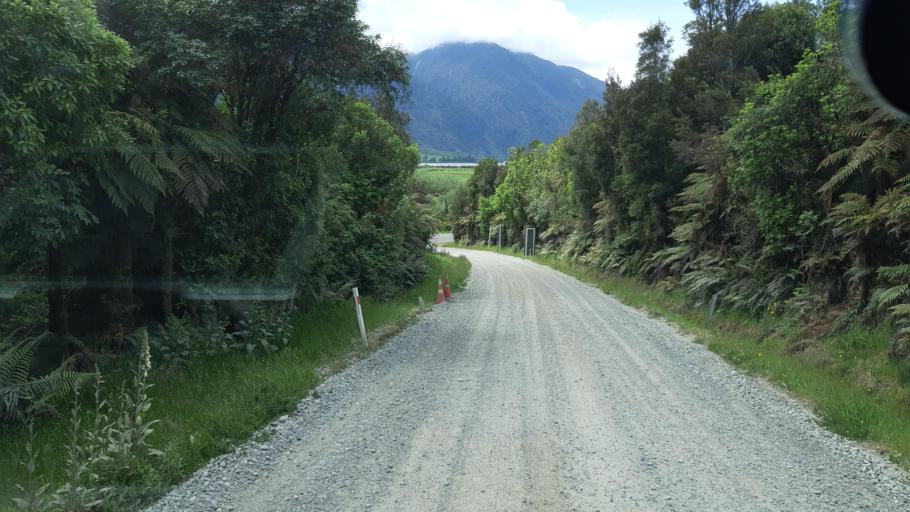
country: NZ
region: West Coast
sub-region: Grey District
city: Greymouth
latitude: -42.7192
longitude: 171.2465
